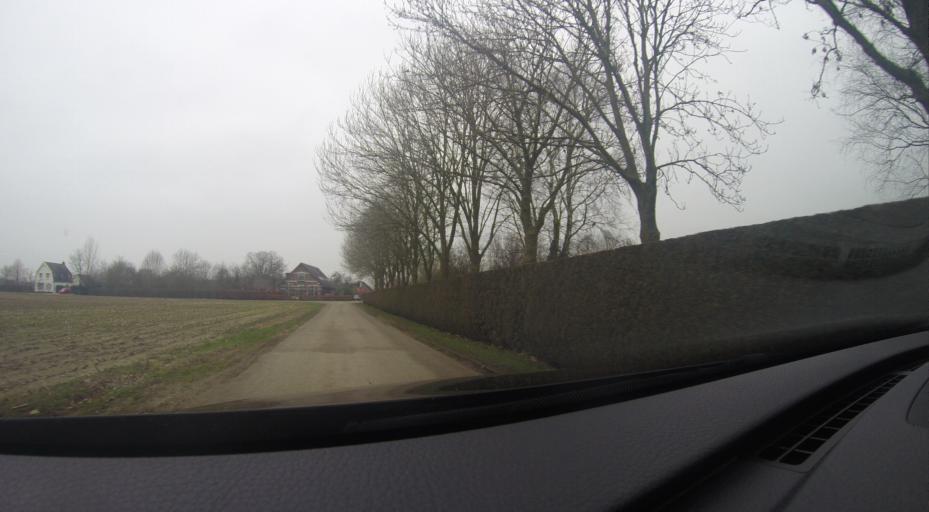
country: NL
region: Gelderland
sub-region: Gemeente Brummen
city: Brummen
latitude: 52.0966
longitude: 6.1758
